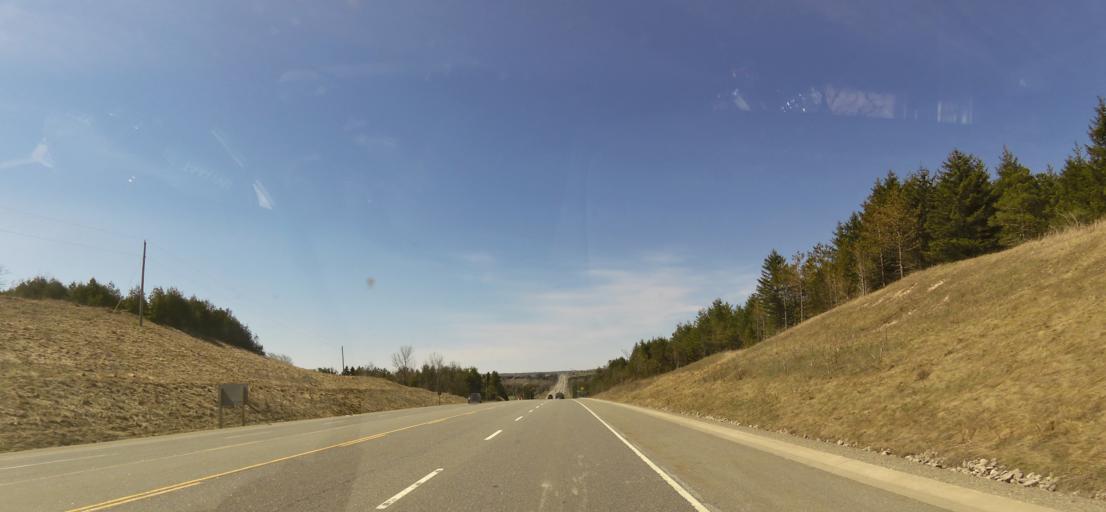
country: CA
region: Ontario
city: Orangeville
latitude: 43.8980
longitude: -80.0471
